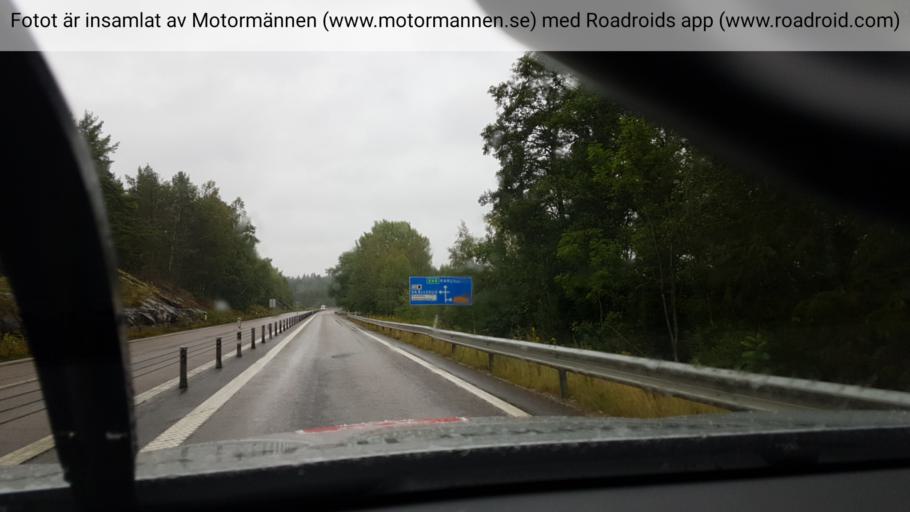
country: SE
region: Vaestra Goetaland
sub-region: Melleruds Kommun
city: Mellerud
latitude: 58.7597
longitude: 12.4904
